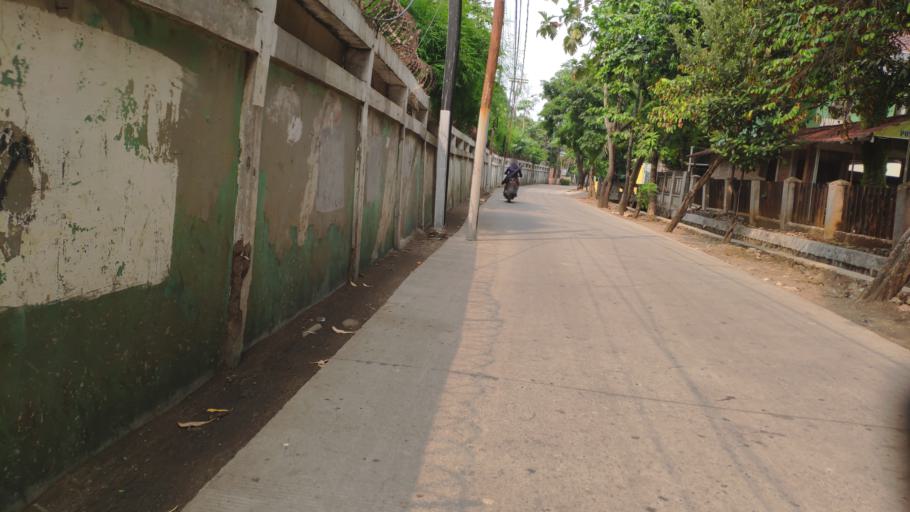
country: ID
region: West Java
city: Depok
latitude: -6.3509
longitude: 106.8077
